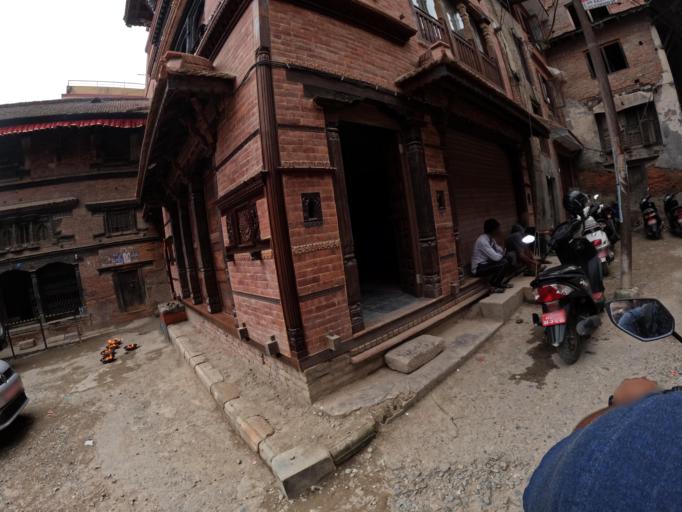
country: NP
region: Central Region
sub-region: Bagmati Zone
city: Bhaktapur
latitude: 27.6842
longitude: 85.3853
